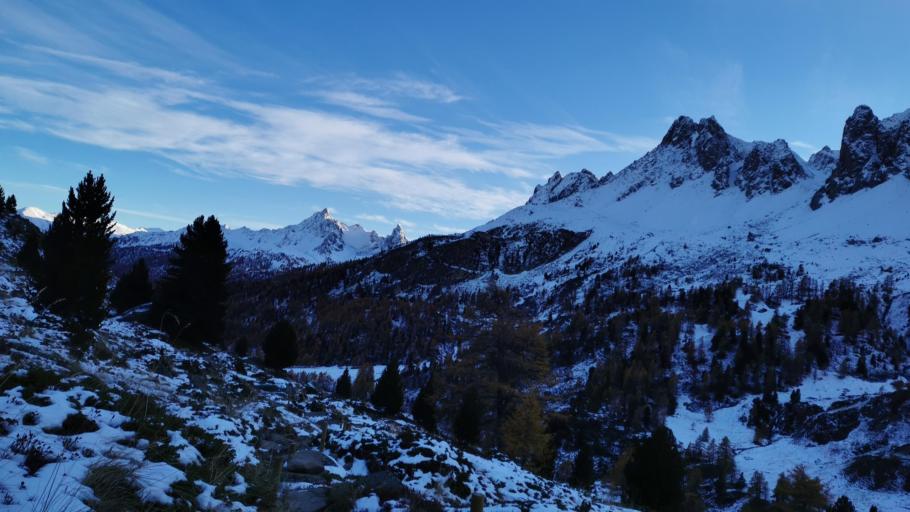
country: FR
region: Provence-Alpes-Cote d'Azur
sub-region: Departement des Hautes-Alpes
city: Le Monetier-les-Bains
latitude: 45.0692
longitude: 6.5178
